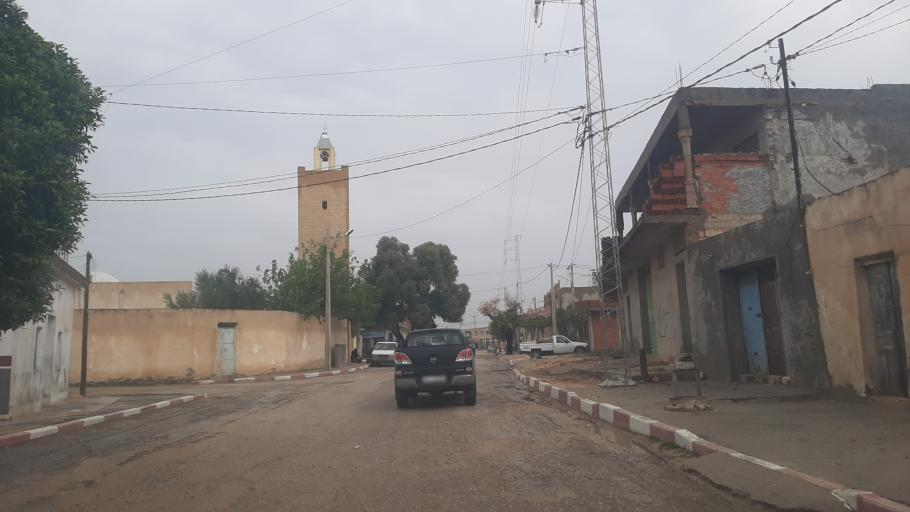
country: TN
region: Al Munastir
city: Sidi Bin Nur
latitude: 35.4796
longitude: 10.8733
